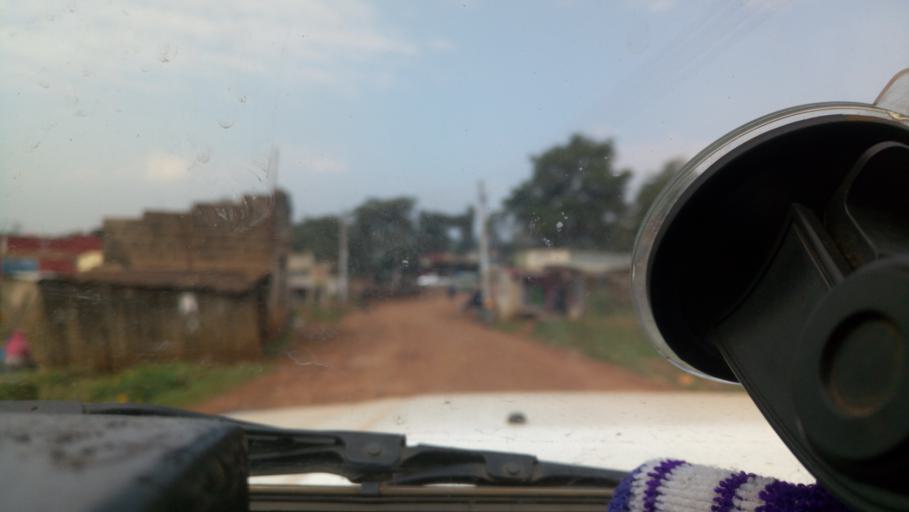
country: KE
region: Kericho
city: Litein
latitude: -0.6262
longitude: 35.1972
